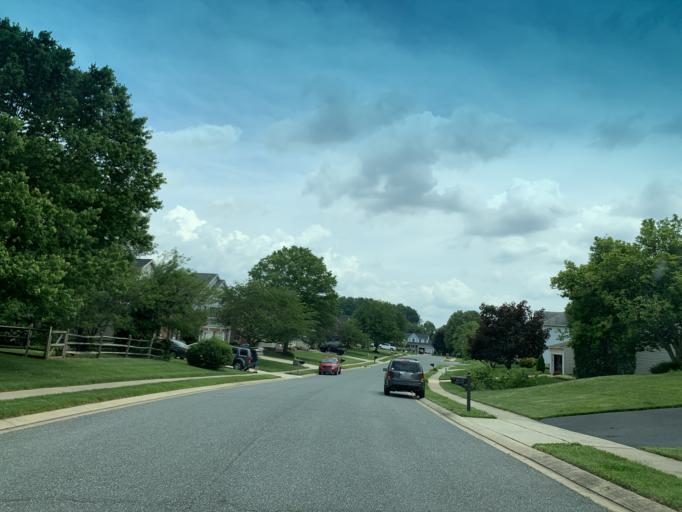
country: US
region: Maryland
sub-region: Harford County
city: South Bel Air
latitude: 39.5549
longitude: -76.3322
